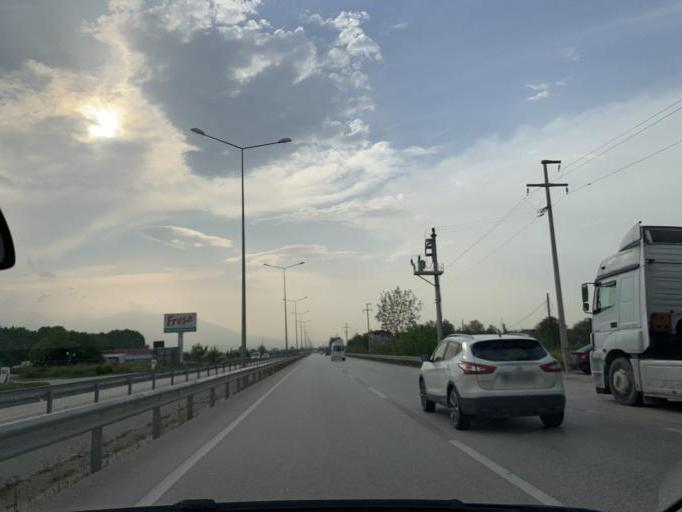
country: TR
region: Bursa
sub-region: Inegoel
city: Inegol
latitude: 40.0618
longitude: 29.5770
